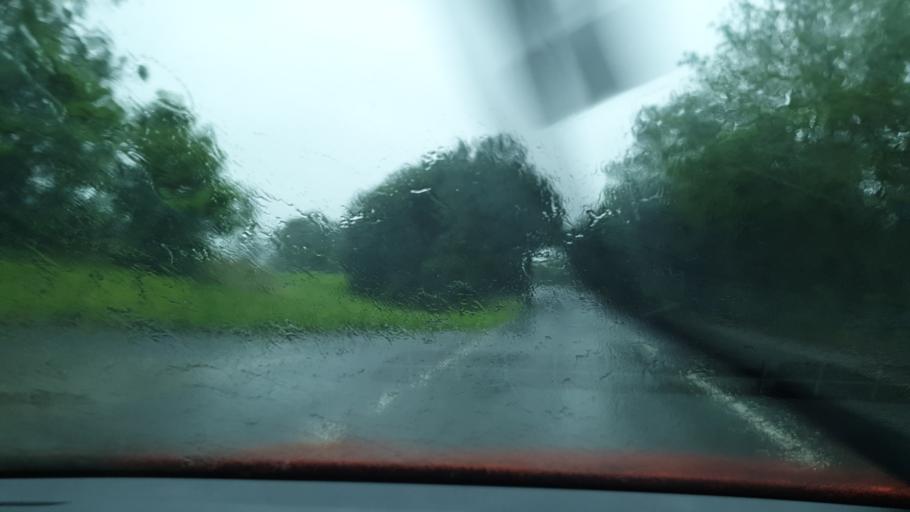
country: GB
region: England
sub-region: Cumbria
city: Millom
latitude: 54.2674
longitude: -3.2154
